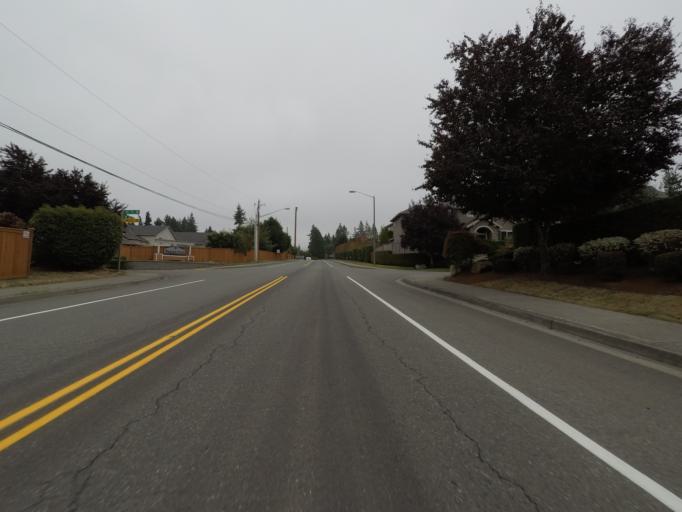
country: US
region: Washington
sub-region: King County
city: Bothell
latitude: 47.7749
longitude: -122.2253
